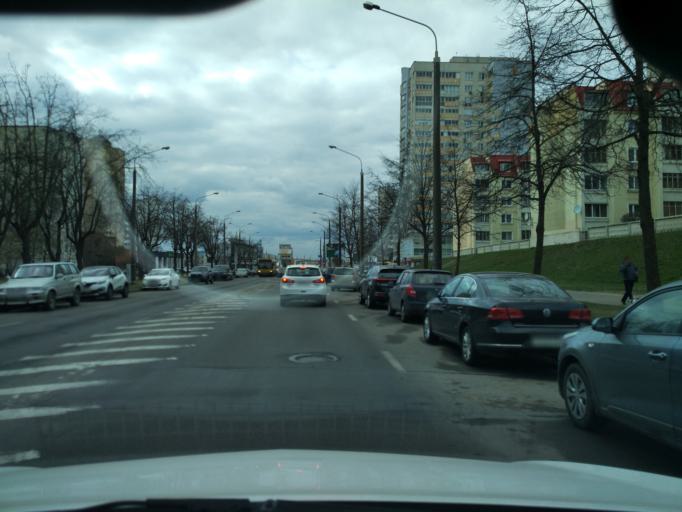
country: BY
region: Minsk
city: Minsk
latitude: 53.9344
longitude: 27.5856
